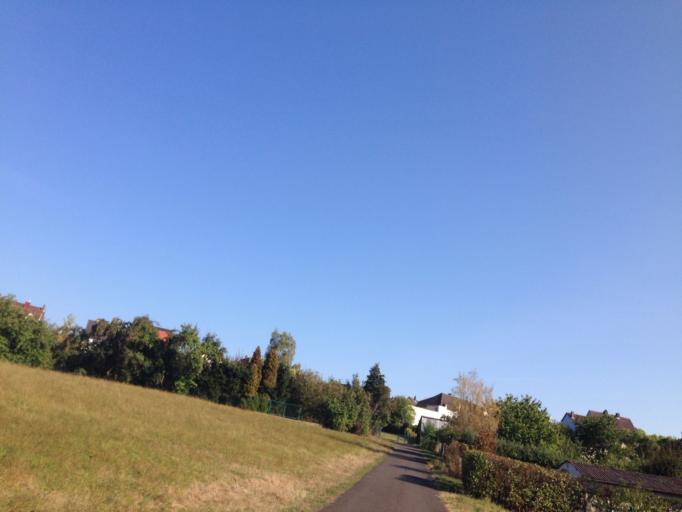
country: DE
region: Hesse
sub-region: Regierungsbezirk Giessen
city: Langgons
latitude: 50.5378
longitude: 8.7168
